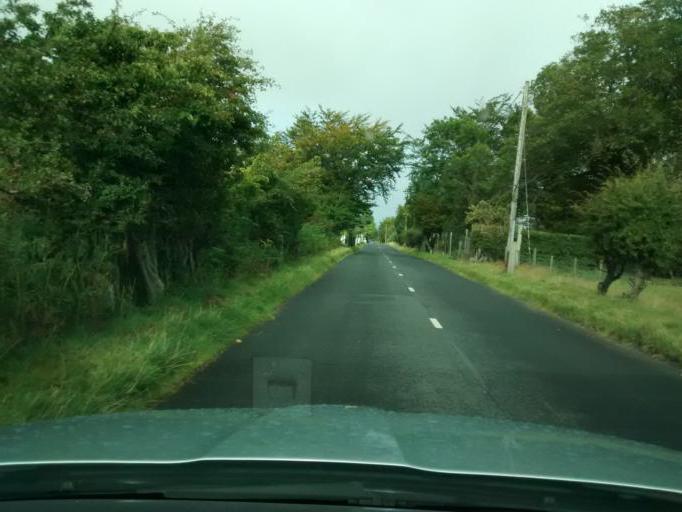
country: GB
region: Scotland
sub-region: North Ayrshire
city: Isle of Arran
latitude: 55.6994
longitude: -5.2782
